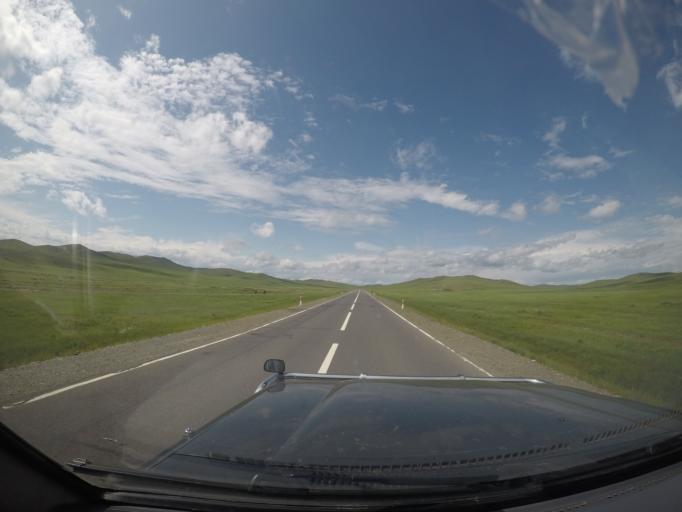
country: MN
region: Hentiy
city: Bayanbulag
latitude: 47.4253
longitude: 109.8538
